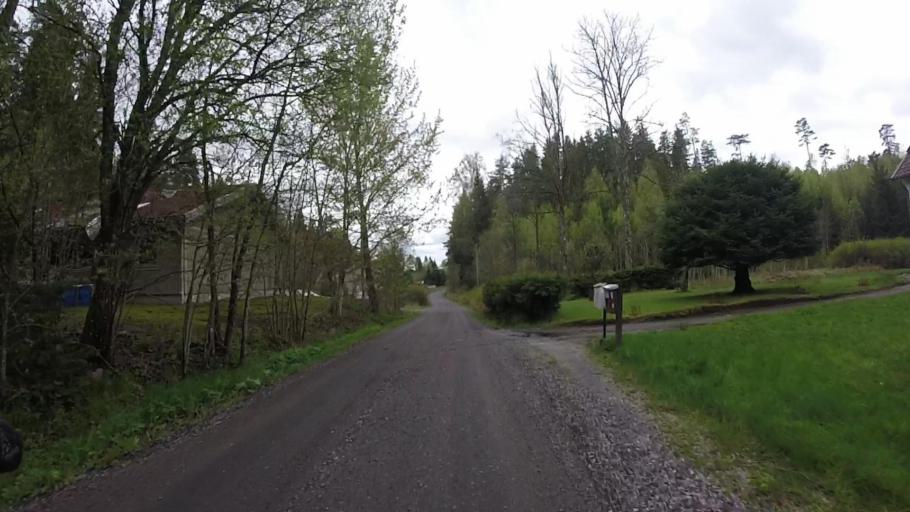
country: SE
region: Vaestra Goetaland
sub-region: Trollhattan
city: Sjuntorp
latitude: 58.2081
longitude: 12.2114
